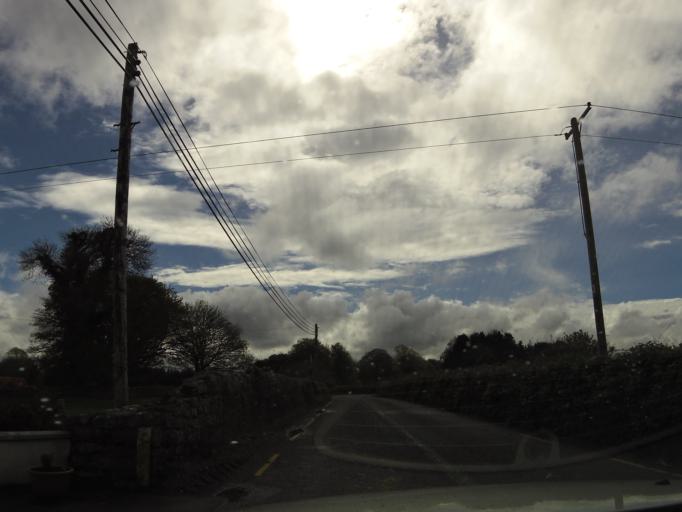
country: IE
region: Connaught
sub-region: Maigh Eo
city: Ballinrobe
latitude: 53.5517
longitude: -9.2616
